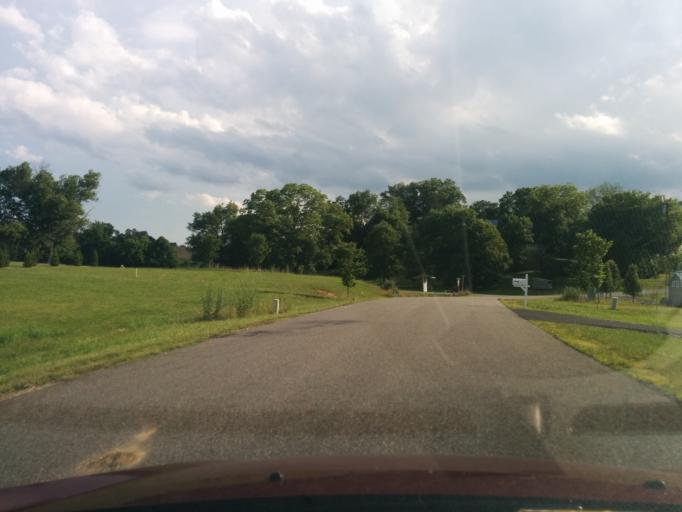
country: US
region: Virginia
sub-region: Rockbridge County
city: East Lexington
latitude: 37.7917
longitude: -79.4077
